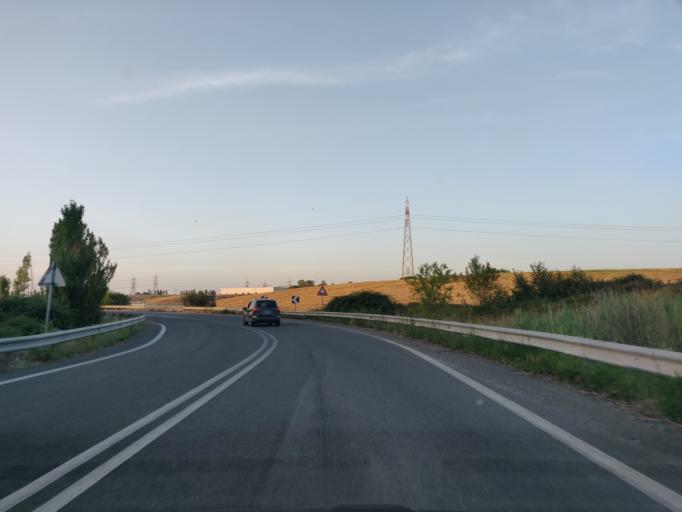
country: IT
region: Latium
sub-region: Citta metropolitana di Roma Capitale
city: Aurelia
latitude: 42.1570
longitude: 11.7903
